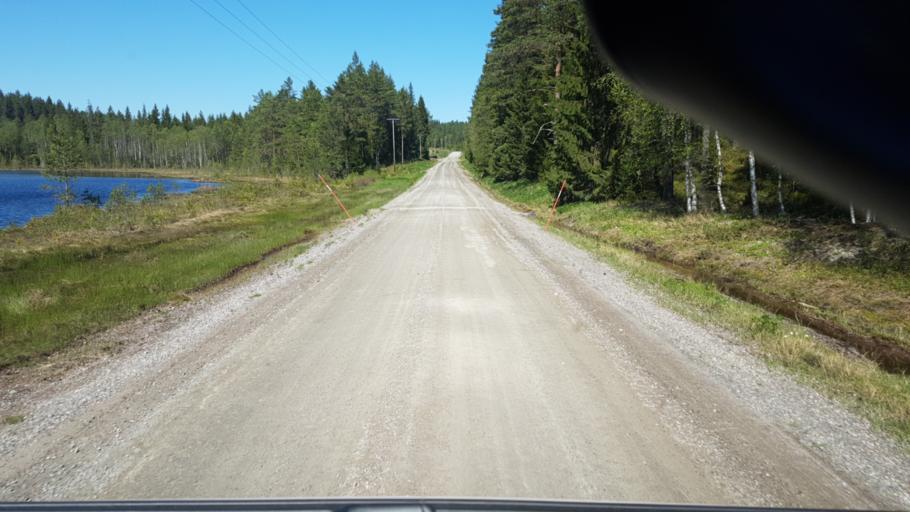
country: SE
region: Vaermland
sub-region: Arvika Kommun
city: Arvika
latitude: 59.8635
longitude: 12.7137
